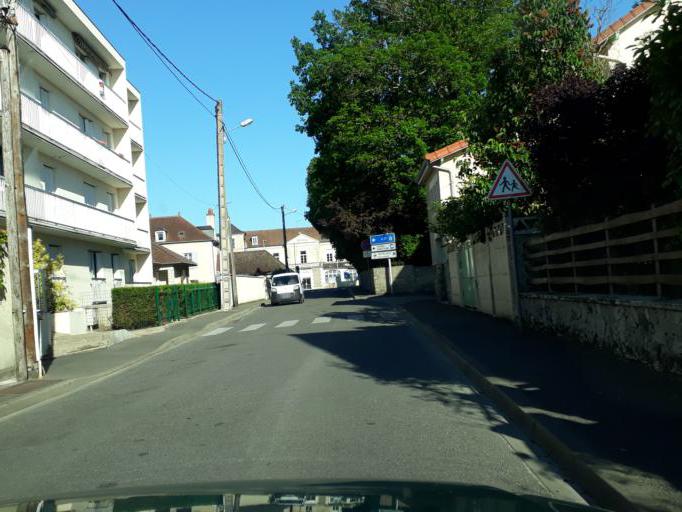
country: FR
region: Bourgogne
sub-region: Departement de la Nievre
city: Cosne-Cours-sur-Loire
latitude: 47.4158
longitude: 2.9260
